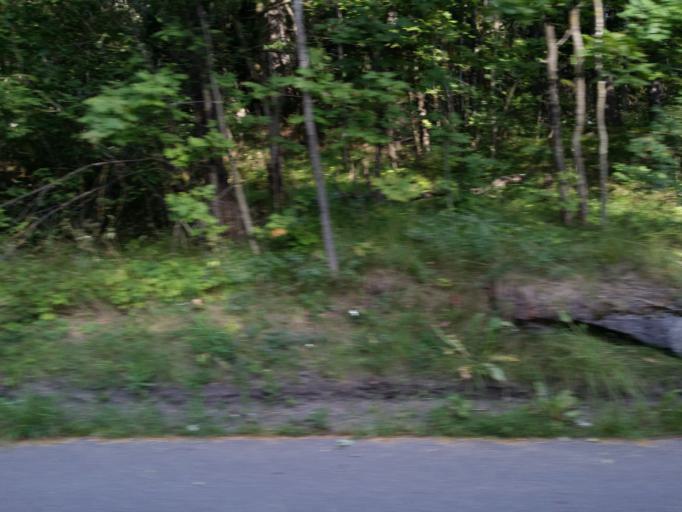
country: NO
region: Akershus
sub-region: Oppegard
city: Kolbotn
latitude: 59.8819
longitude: 10.8406
